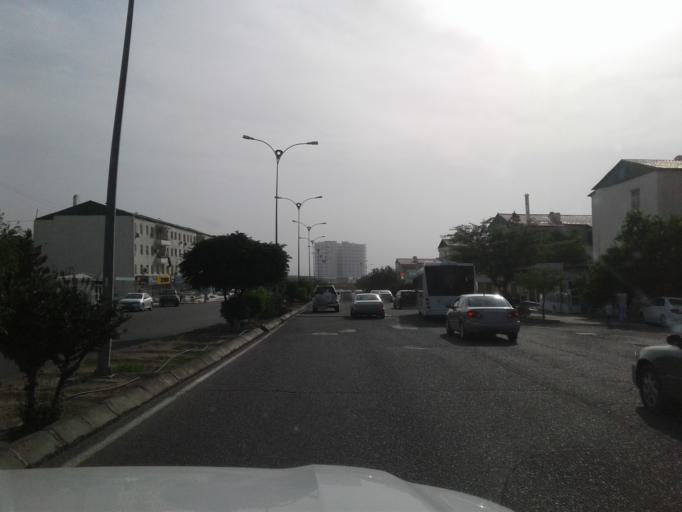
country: TM
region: Balkan
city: Turkmenbasy
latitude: 40.0005
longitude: 52.9721
